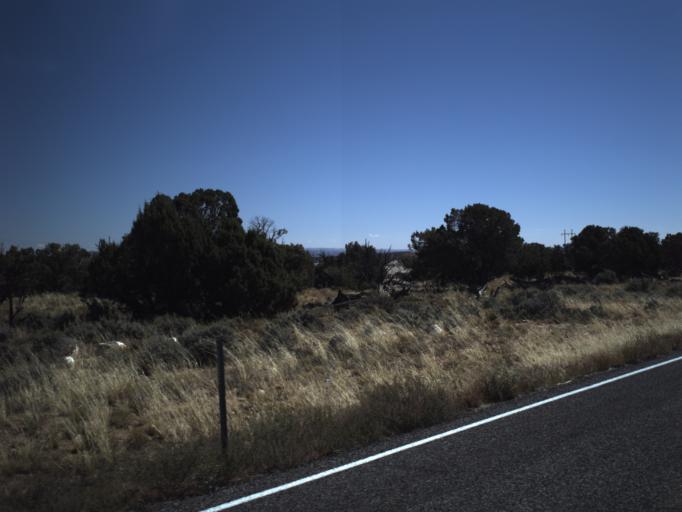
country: US
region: Utah
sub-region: Wayne County
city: Loa
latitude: 37.8477
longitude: -111.4280
